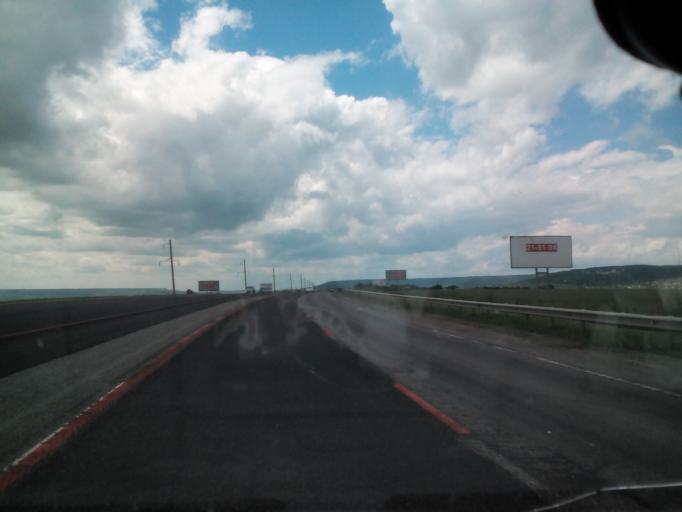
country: RU
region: Stavropol'skiy
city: Tatarka
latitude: 44.9535
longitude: 41.9828
